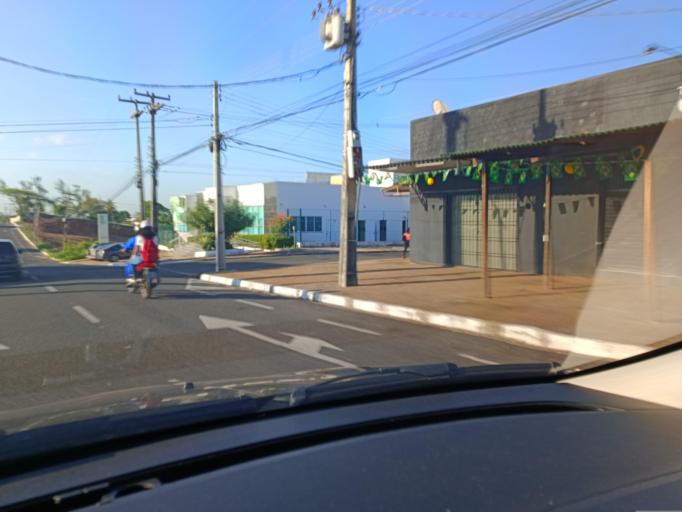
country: BR
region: Piaui
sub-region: Teresina
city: Teresina
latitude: -5.0757
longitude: -42.7516
